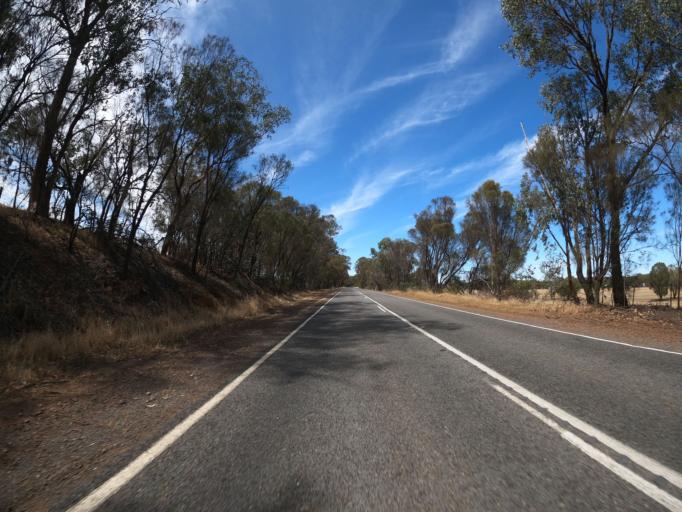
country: AU
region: Victoria
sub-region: Benalla
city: Benalla
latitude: -36.3380
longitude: 145.9590
